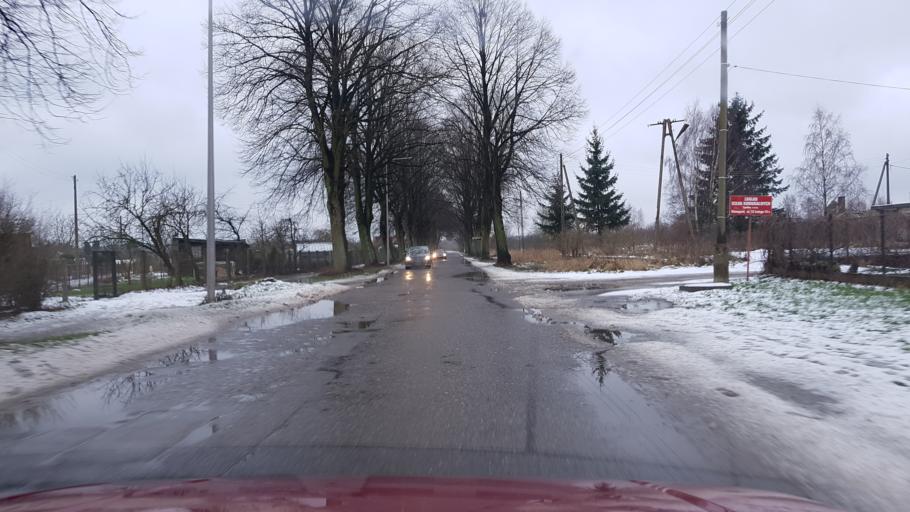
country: PL
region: West Pomeranian Voivodeship
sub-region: Powiat goleniowski
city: Nowogard
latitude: 53.6613
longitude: 15.1249
